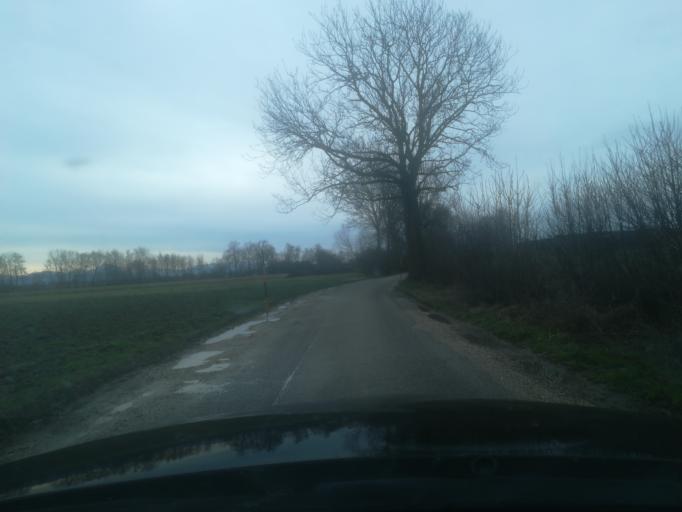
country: AT
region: Upper Austria
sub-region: Wels-Land
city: Gunskirchen
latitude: 48.1664
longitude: 13.9717
